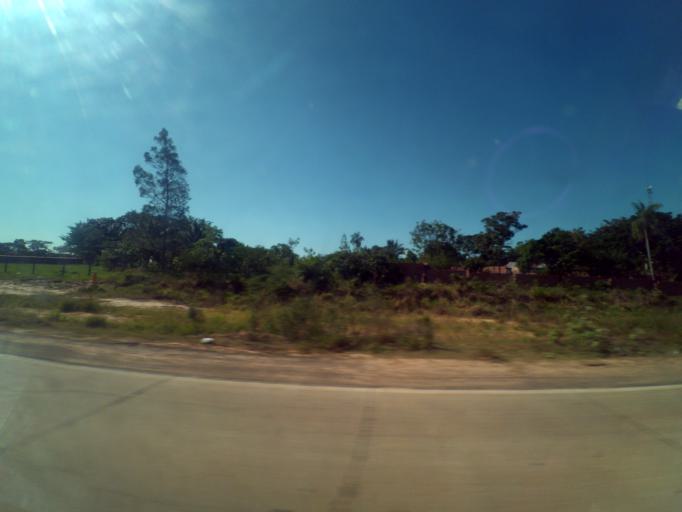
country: BO
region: Santa Cruz
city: Santa Cruz de la Sierra
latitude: -17.7750
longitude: -63.2464
